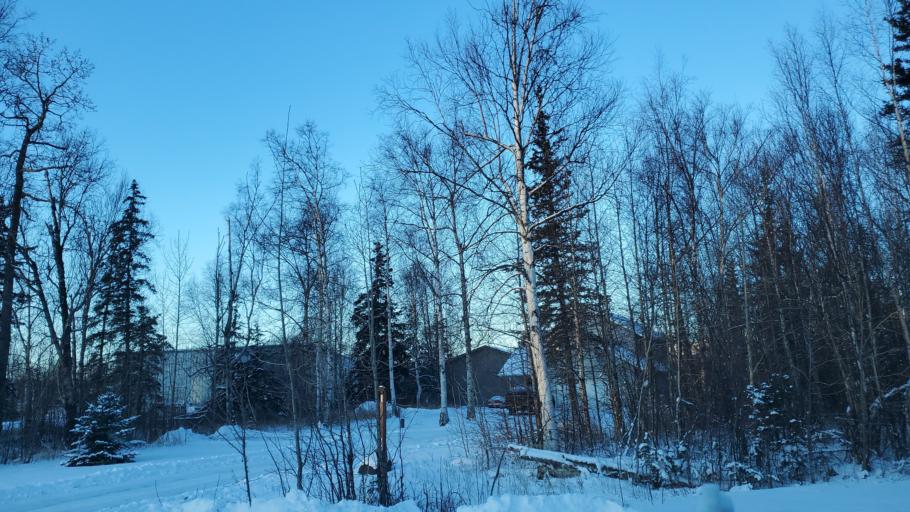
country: US
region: Alaska
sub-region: Matanuska-Susitna Borough
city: Lakes
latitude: 61.6381
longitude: -149.2980
